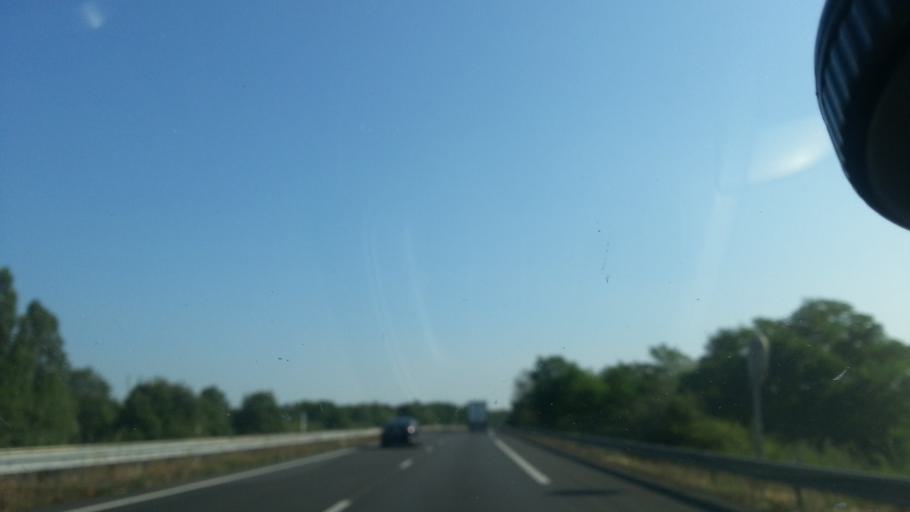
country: FR
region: Centre
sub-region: Departement d'Indre-et-Loire
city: La Celle-Saint-Avant
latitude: 47.0319
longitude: 0.5713
